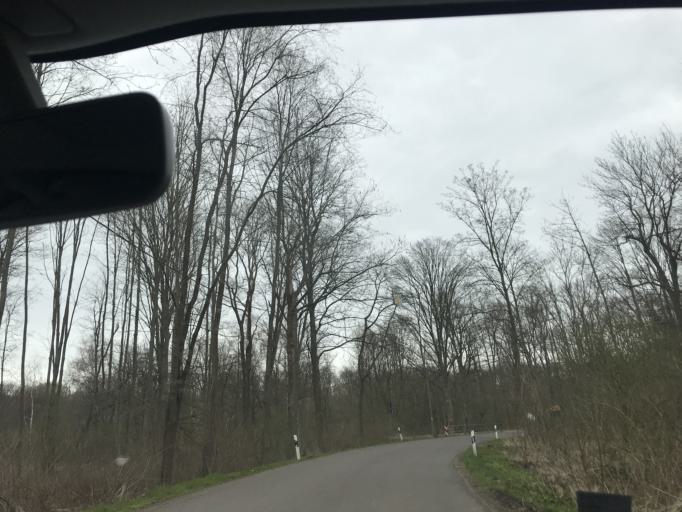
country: DE
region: Saxony
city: Schkeuditz
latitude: 51.3715
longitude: 12.2568
